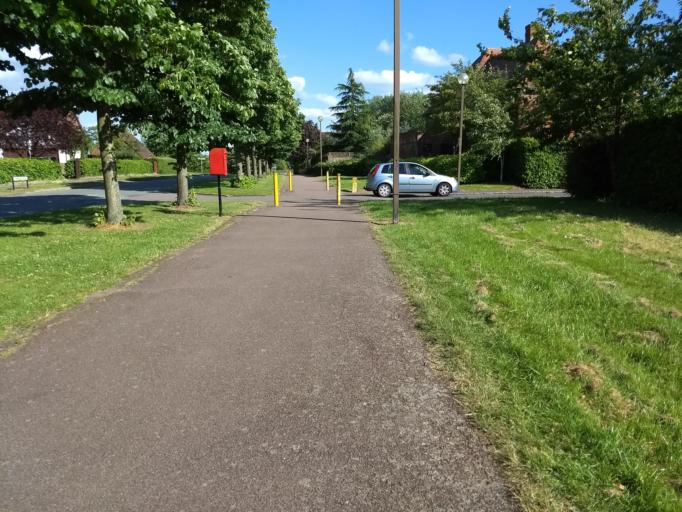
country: GB
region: England
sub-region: Milton Keynes
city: Shenley Church End
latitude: 52.0216
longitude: -0.7819
